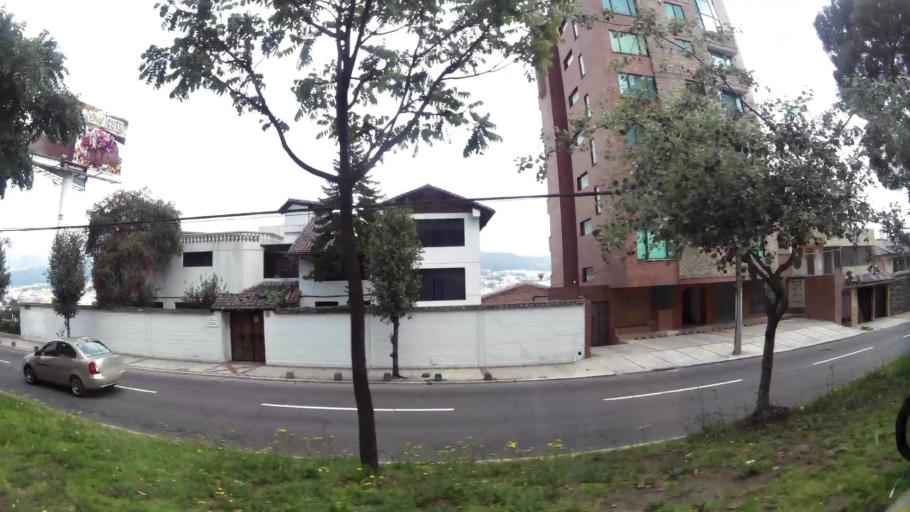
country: EC
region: Pichincha
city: Quito
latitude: -0.1752
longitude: -78.4723
